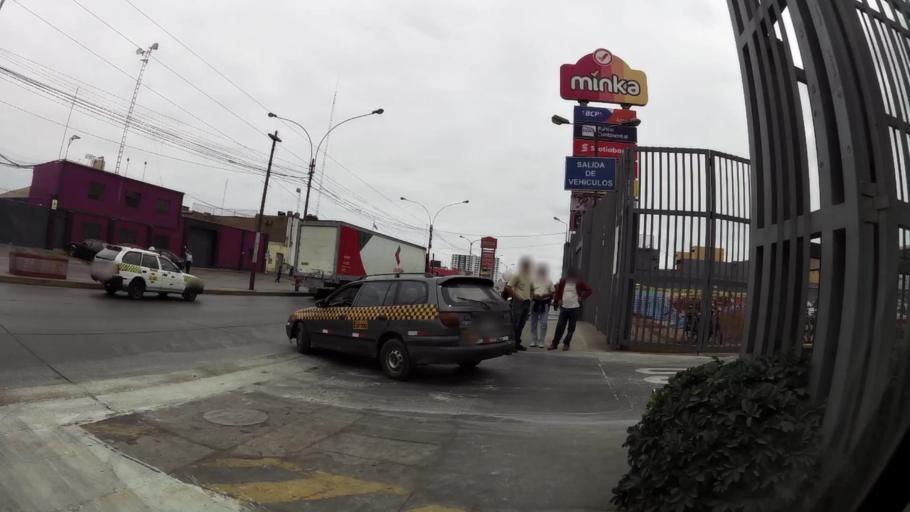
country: PE
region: Callao
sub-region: Callao
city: Callao
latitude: -12.0495
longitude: -77.1117
